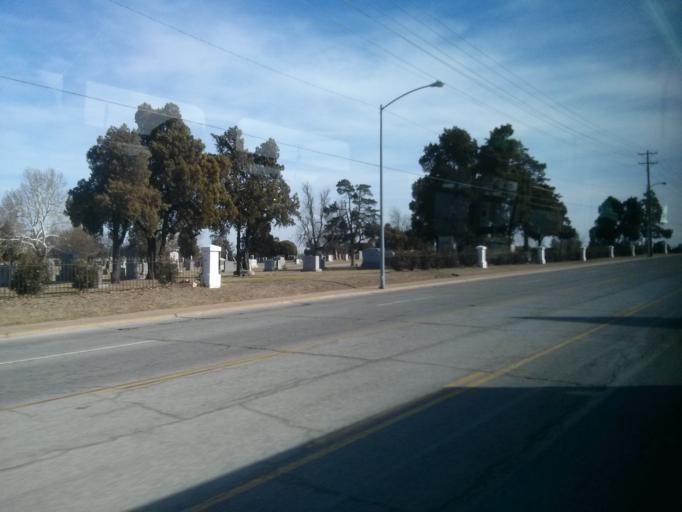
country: US
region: Oklahoma
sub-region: Tulsa County
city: Tulsa
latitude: 36.1606
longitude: -95.9306
